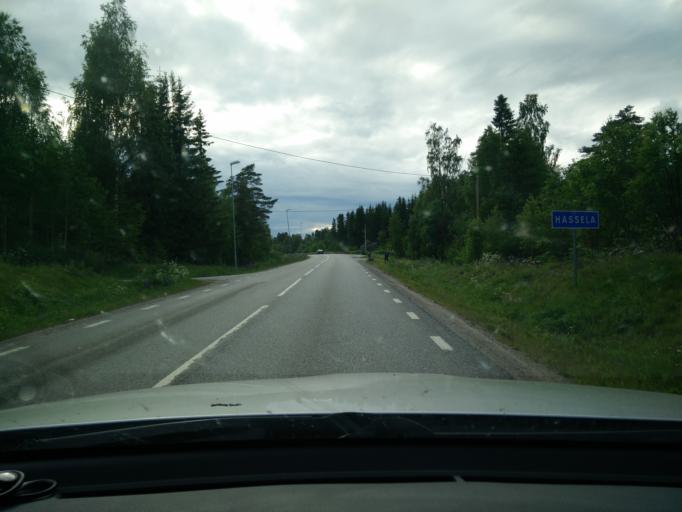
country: SE
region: Gaevleborg
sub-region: Nordanstigs Kommun
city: Bergsjoe
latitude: 62.0991
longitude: 16.7450
